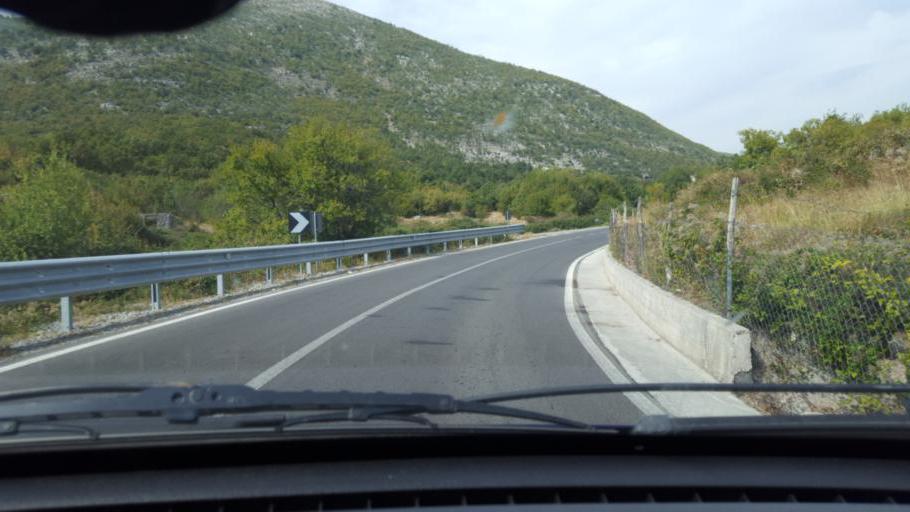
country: AL
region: Shkoder
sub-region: Rrethi i Malesia e Madhe
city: Kastrat
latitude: 42.3845
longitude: 19.4920
